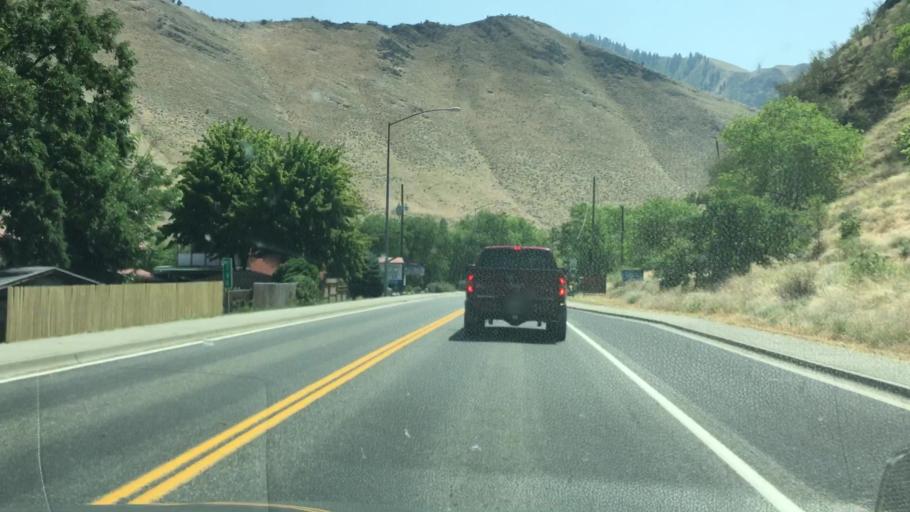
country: US
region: Idaho
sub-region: Idaho County
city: Grangeville
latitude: 45.4294
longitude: -116.3126
